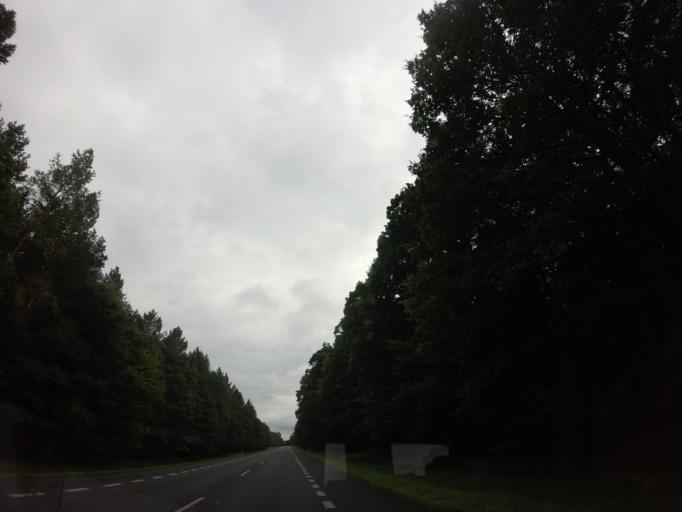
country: PL
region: West Pomeranian Voivodeship
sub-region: Powiat goleniowski
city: Przybiernow
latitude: 53.7262
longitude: 14.7738
